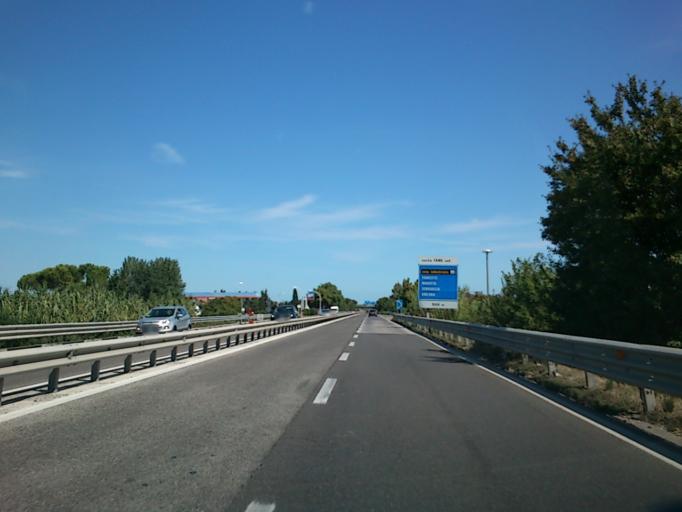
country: IT
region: The Marches
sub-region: Provincia di Pesaro e Urbino
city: Bellocchi
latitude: 43.8001
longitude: 13.0099
